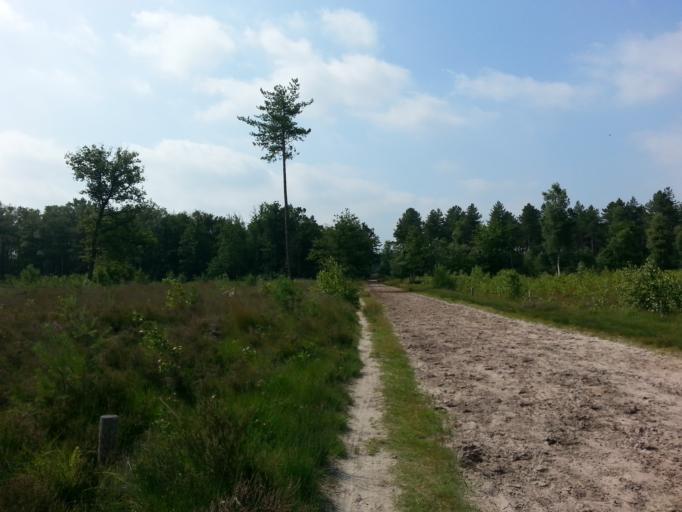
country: NL
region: Utrecht
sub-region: Gemeente Utrechtse Heuvelrug
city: Maarn
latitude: 52.0951
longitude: 5.3793
